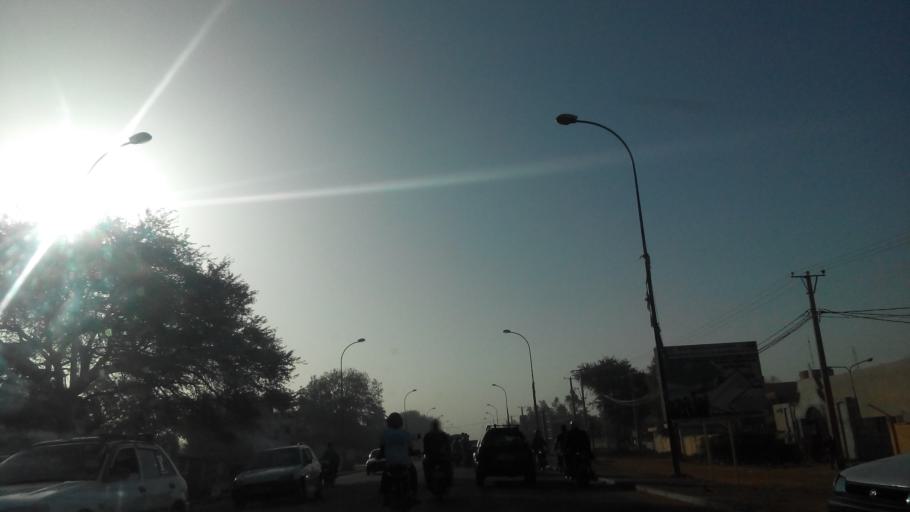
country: NE
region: Niamey
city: Niamey
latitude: 13.5378
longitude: 2.0764
